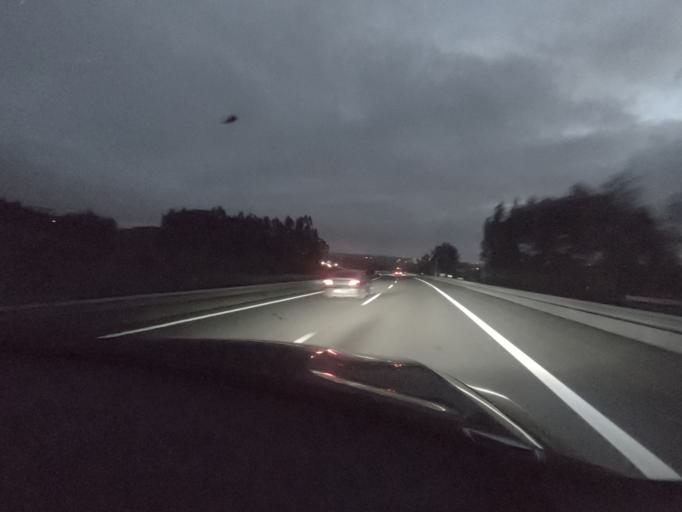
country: PT
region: Leiria
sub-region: Leiria
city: Caranguejeira
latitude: 39.7758
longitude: -8.7426
